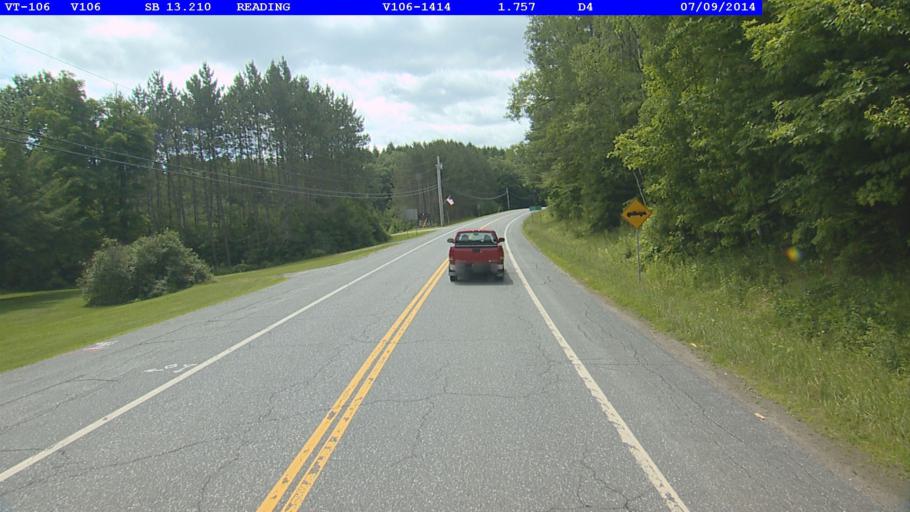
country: US
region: Vermont
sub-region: Windsor County
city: Windsor
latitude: 43.4688
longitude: -72.5331
